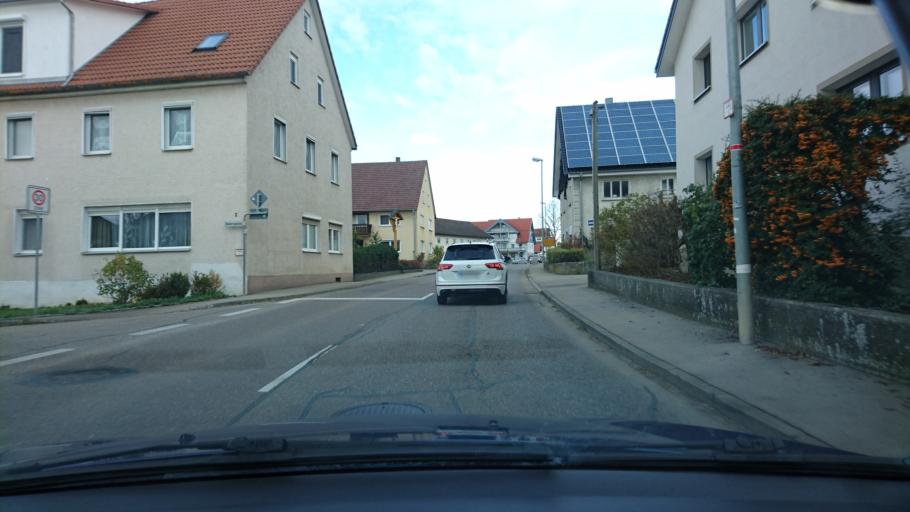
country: DE
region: Baden-Wuerttemberg
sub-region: Regierungsbezirk Stuttgart
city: Neresheim
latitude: 48.7931
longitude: 10.2641
